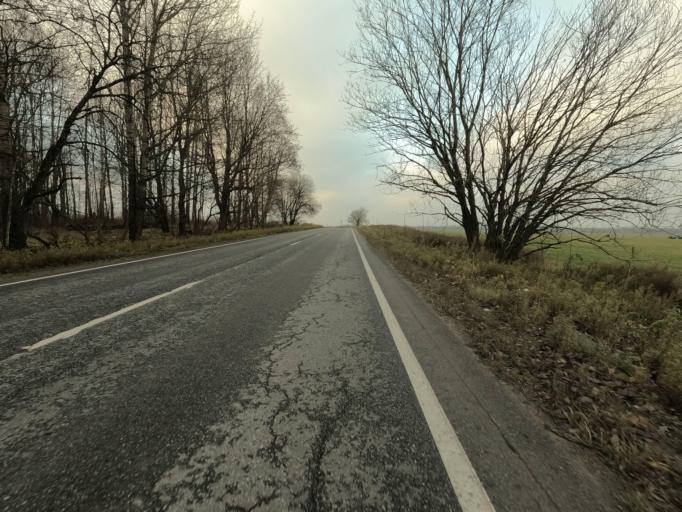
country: RU
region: Leningrad
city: Mga
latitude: 59.7555
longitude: 31.0395
